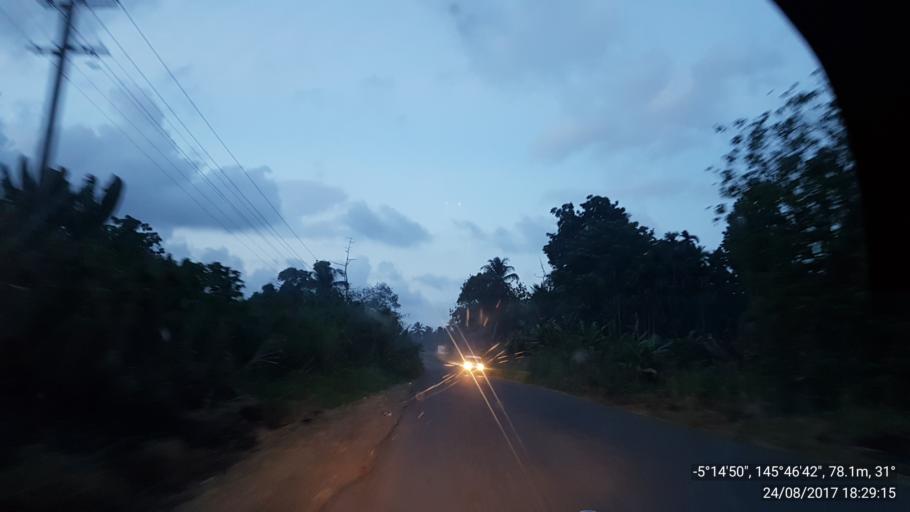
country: PG
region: Madang
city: Madang
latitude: -5.2472
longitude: 145.7786
